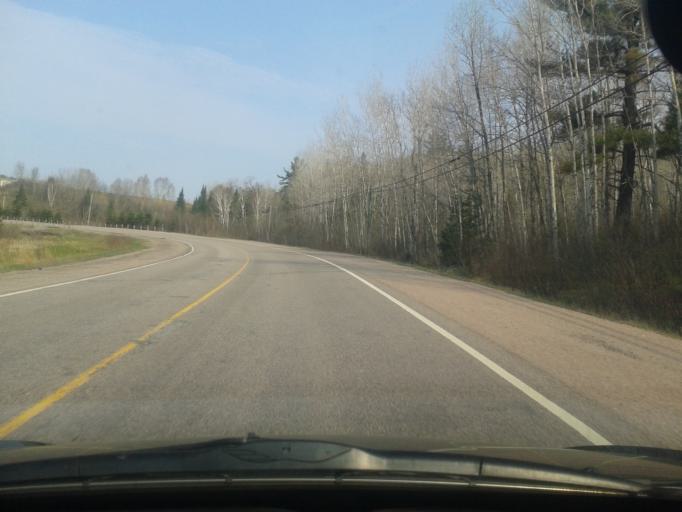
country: CA
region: Ontario
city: Powassan
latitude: 46.1945
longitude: -79.3211
